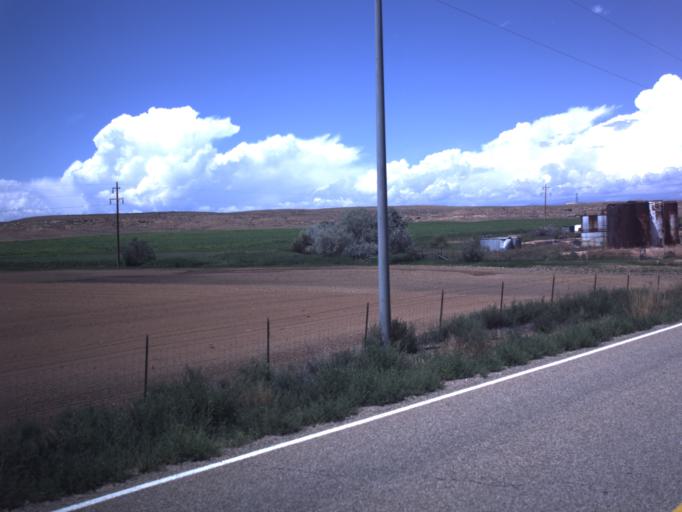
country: US
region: Utah
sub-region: Uintah County
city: Maeser
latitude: 40.2536
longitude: -109.6844
